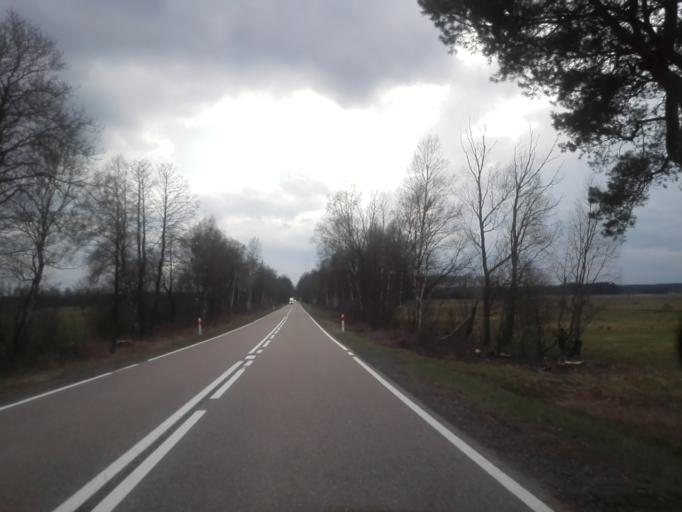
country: PL
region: Podlasie
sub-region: Powiat sejnenski
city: Krasnopol
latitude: 53.9482
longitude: 23.1966
